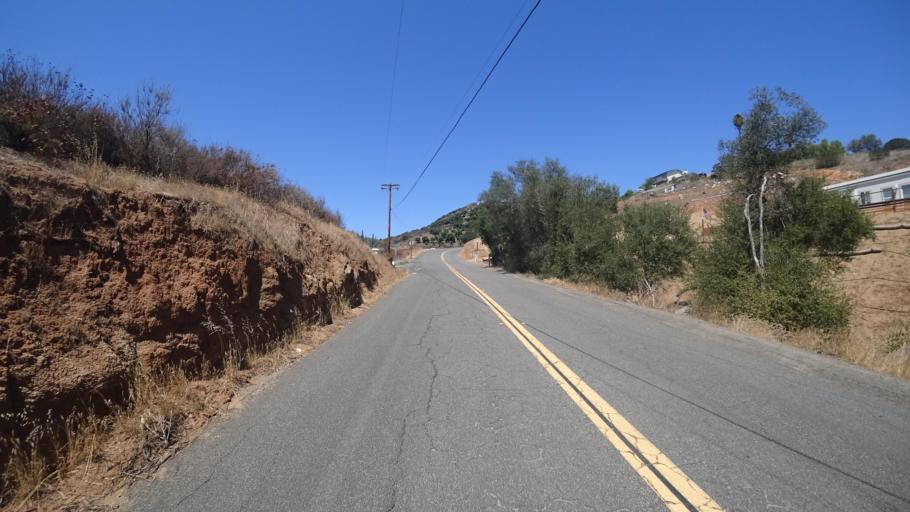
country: US
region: California
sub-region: San Diego County
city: Hidden Meadows
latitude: 33.2995
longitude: -117.0861
